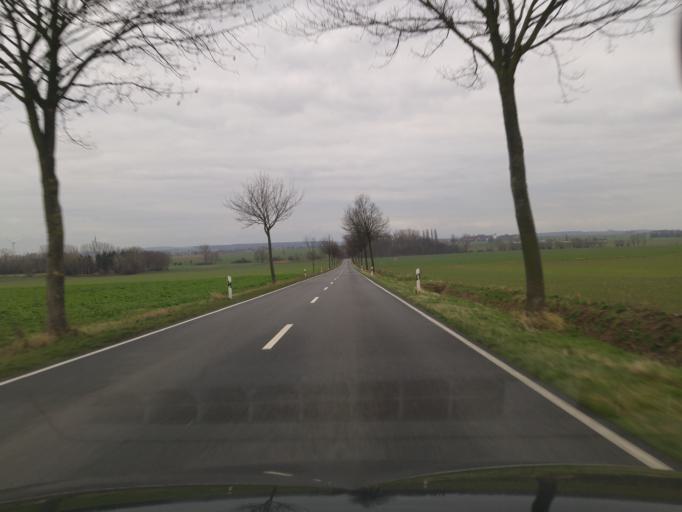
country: DE
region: Lower Saxony
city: Ilsede
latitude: 52.2394
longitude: 10.1696
